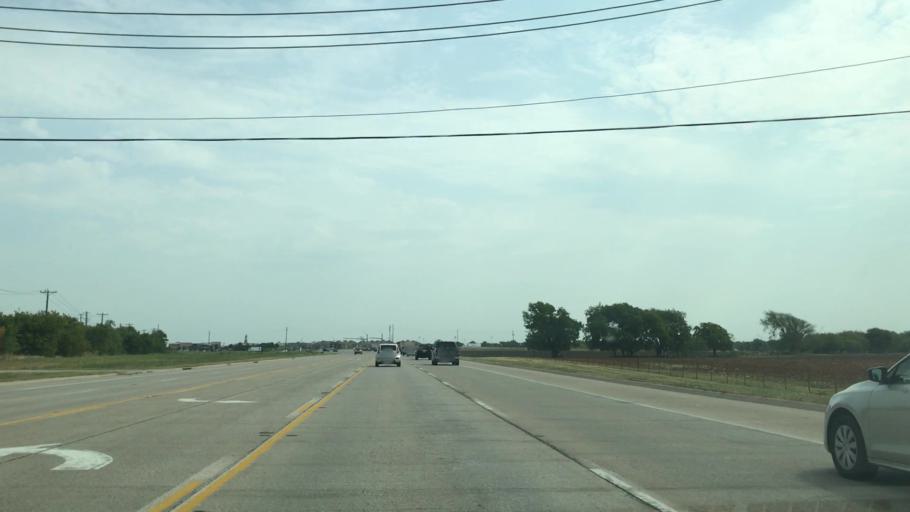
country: US
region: Texas
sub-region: Denton County
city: Roanoke
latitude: 32.9809
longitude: -97.2401
